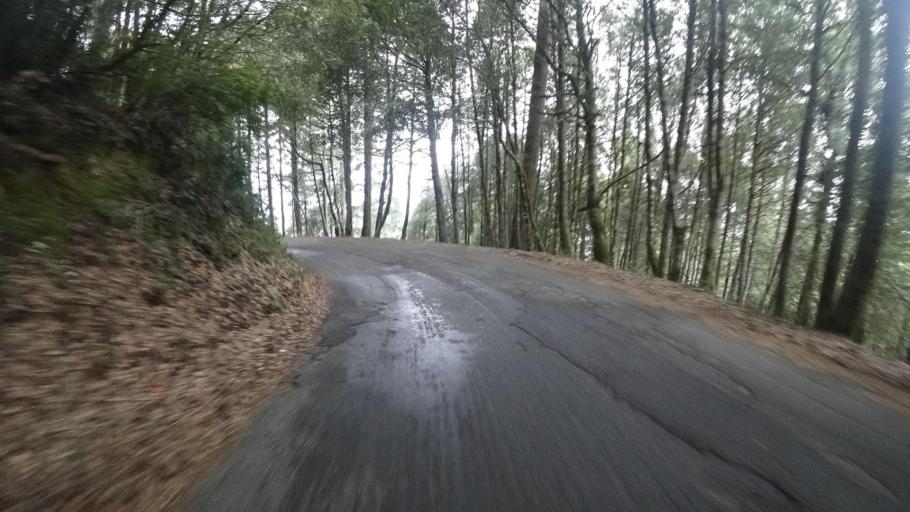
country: US
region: California
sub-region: Humboldt County
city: Redway
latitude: 40.2741
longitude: -123.7709
